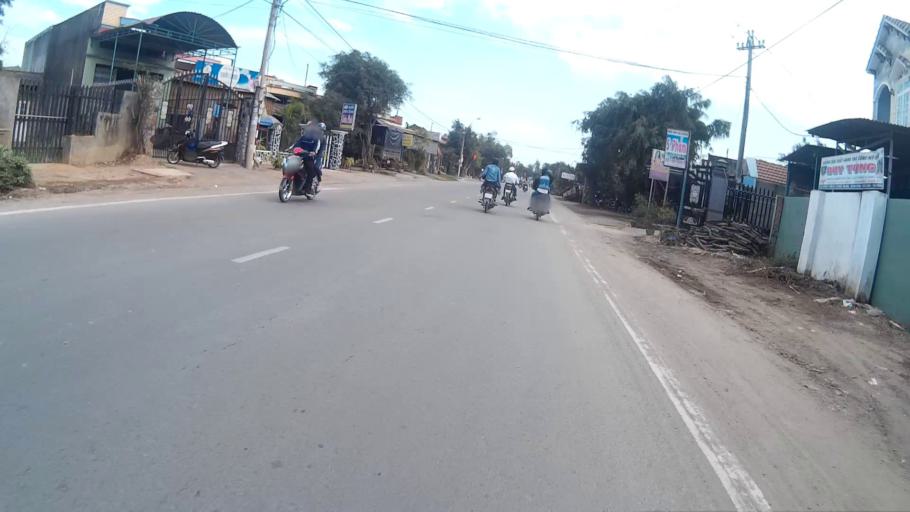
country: VN
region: Binh Dinh
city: An Nhon
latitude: 13.8624
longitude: 109.1334
